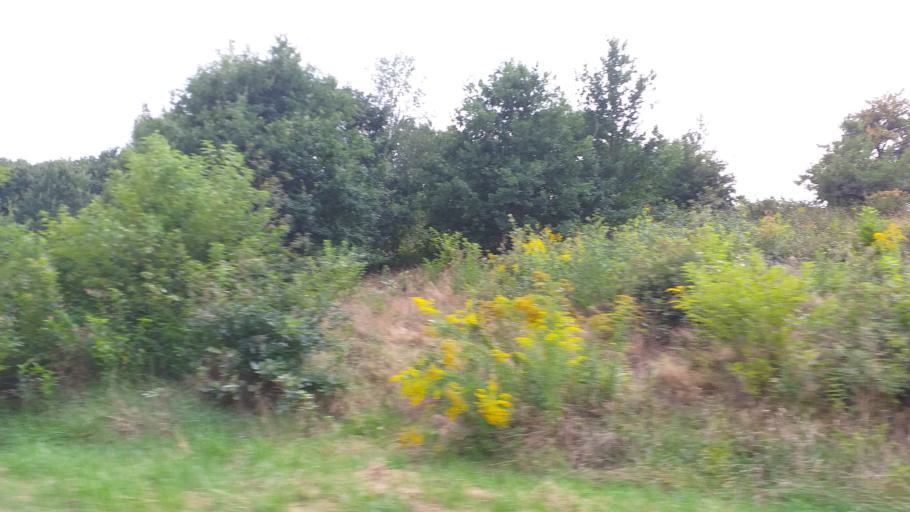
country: PL
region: Lower Silesian Voivodeship
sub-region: Powiat lubanski
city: Lesna
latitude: 51.0452
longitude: 15.2568
